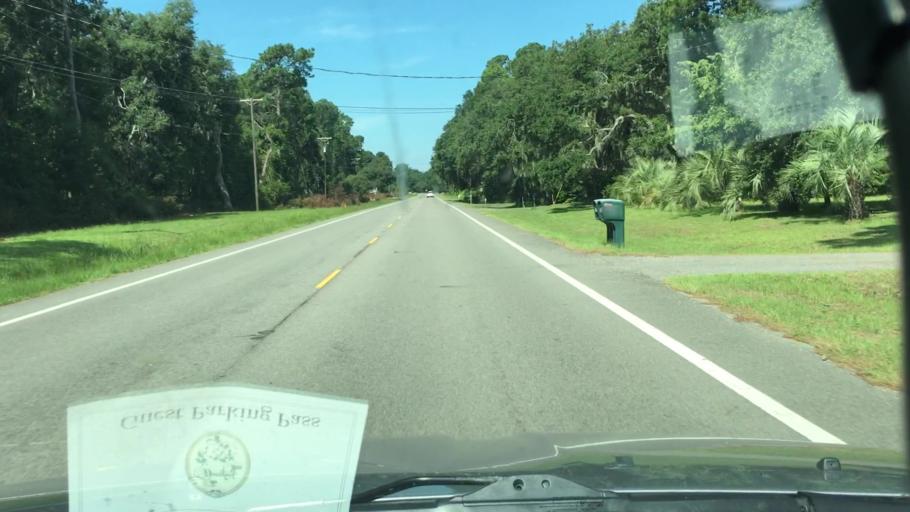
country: US
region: South Carolina
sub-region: Beaufort County
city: Beaufort
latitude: 32.4127
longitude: -80.5125
